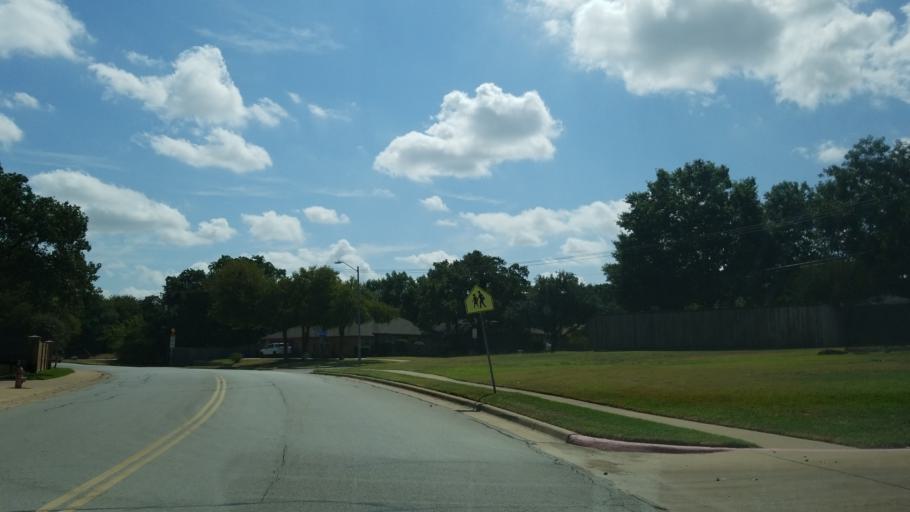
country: US
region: Texas
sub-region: Tarrant County
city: Euless
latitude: 32.8596
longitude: -97.0972
